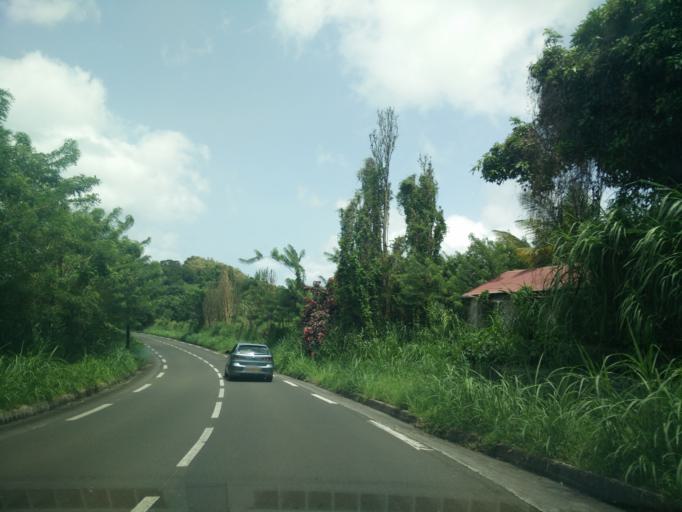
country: MQ
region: Martinique
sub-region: Martinique
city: Le Morne-Rouge
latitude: 14.7670
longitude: -61.1468
